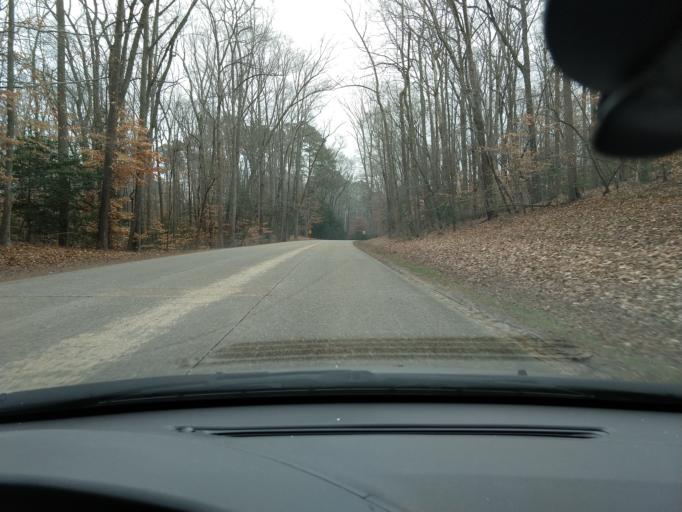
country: US
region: Virginia
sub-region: City of Williamsburg
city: Williamsburg
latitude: 37.2830
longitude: -76.6392
